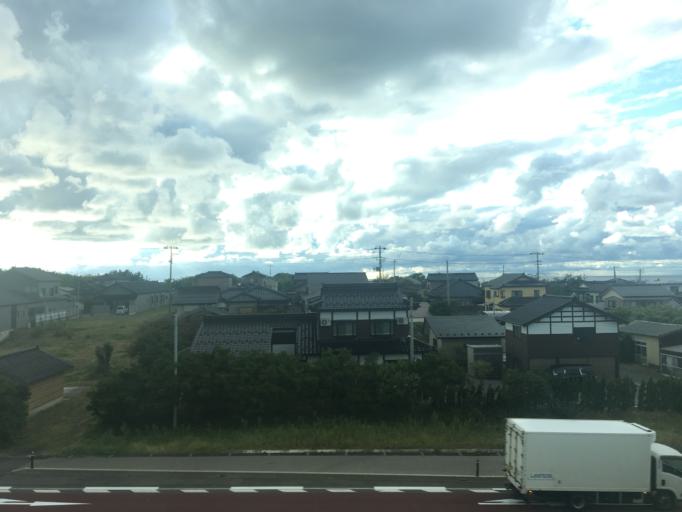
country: JP
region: Akita
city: Akita Shi
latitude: 39.5514
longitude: 140.0563
